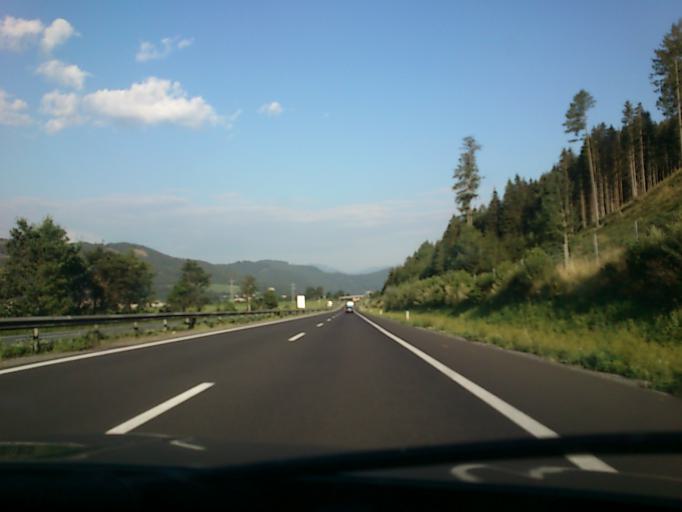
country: AT
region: Styria
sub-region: Politischer Bezirk Leoben
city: Kammern im Liesingtal
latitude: 47.3839
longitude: 14.9265
